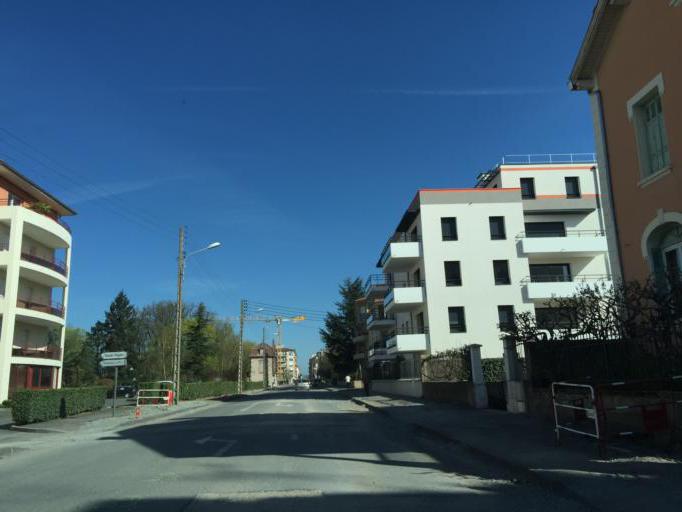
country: FR
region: Rhone-Alpes
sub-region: Departement de la Loire
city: Feurs
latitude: 45.7390
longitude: 4.2245
